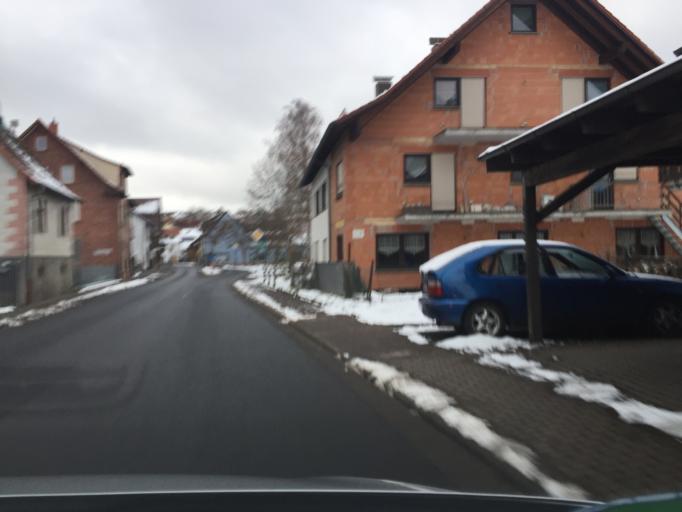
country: DE
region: Bavaria
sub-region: Regierungsbezirk Unterfranken
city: Geiselbach
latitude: 50.1212
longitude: 9.1994
